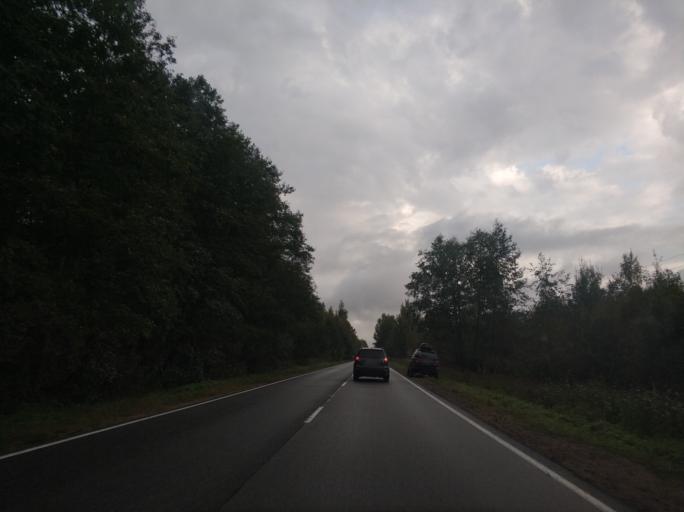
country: RU
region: Leningrad
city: Borisova Griva
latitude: 60.1375
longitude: 30.9562
